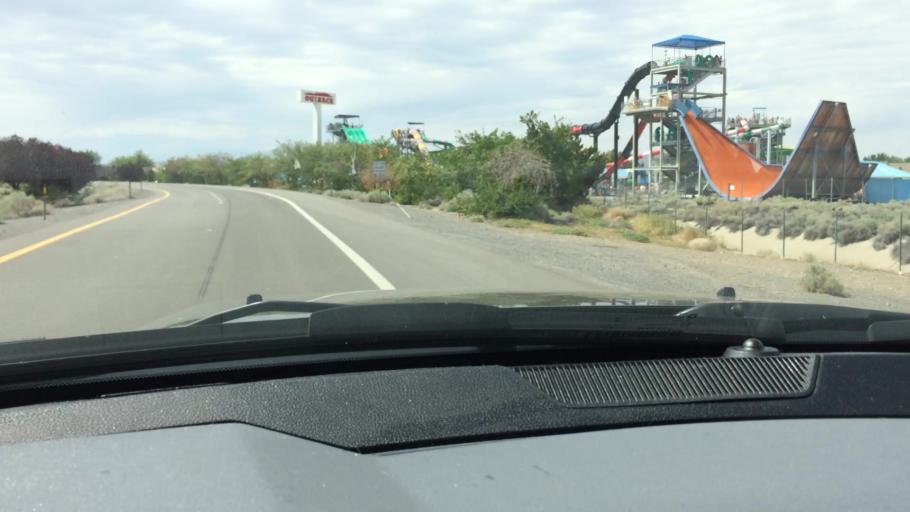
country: US
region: Nevada
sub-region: Washoe County
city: Sparks
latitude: 39.5290
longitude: -119.7125
